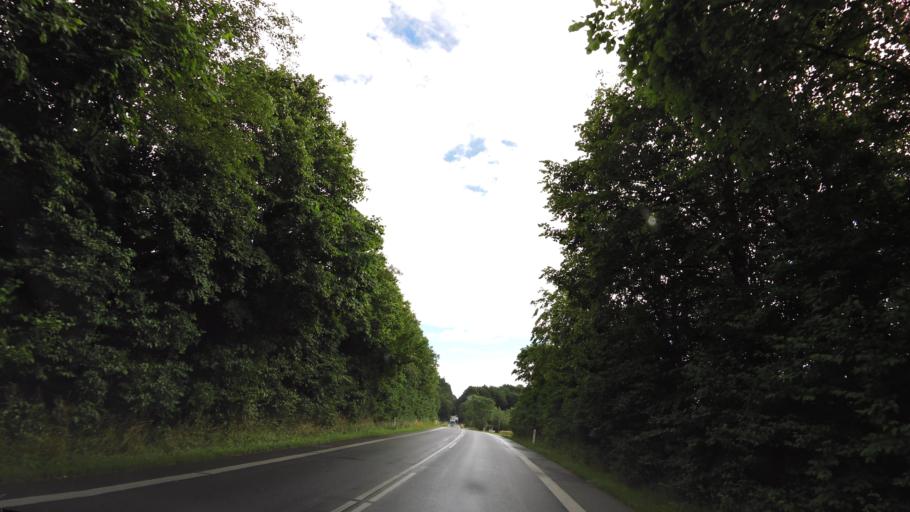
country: DK
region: South Denmark
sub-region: Assens Kommune
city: Vissenbjerg
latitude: 55.4399
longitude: 10.1827
